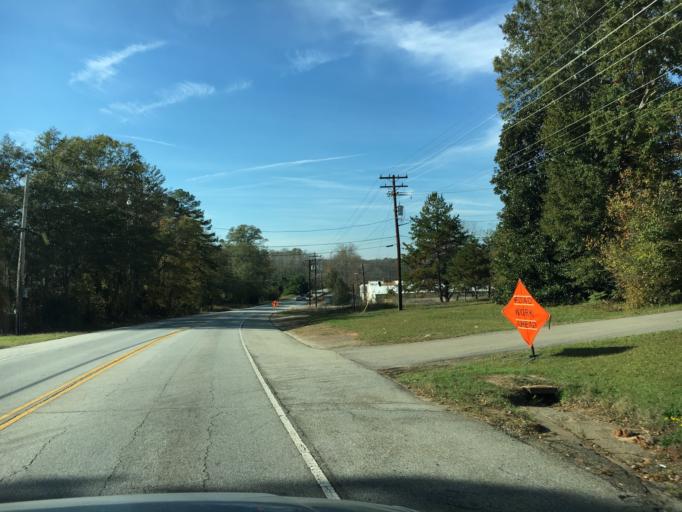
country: US
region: South Carolina
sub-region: Anderson County
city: Anderson
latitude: 34.5036
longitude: -82.6152
